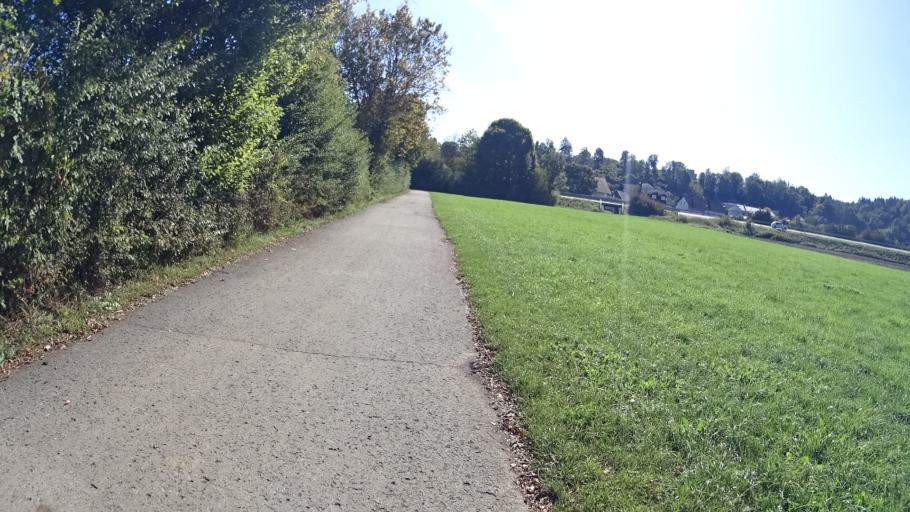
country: DE
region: Bavaria
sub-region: Upper Bavaria
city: Walting
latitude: 48.8894
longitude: 11.2600
